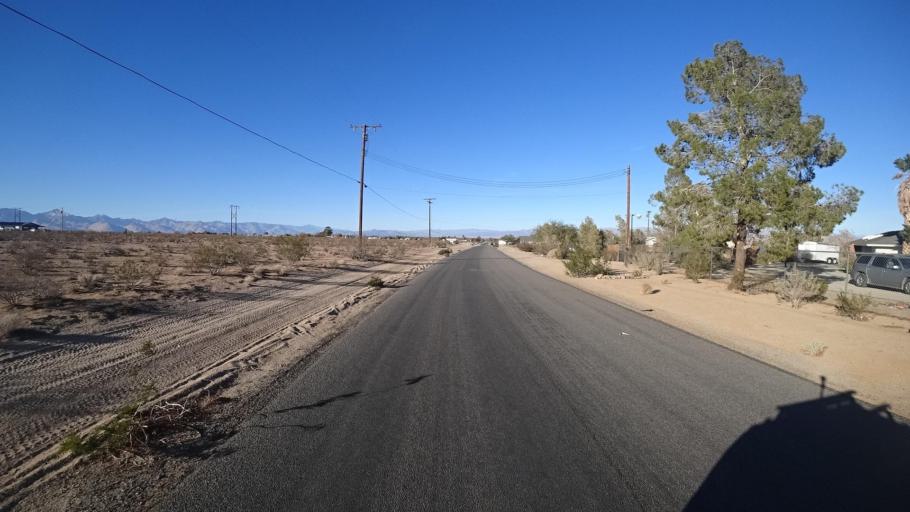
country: US
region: California
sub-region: Kern County
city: Ridgecrest
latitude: 35.5918
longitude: -117.6972
